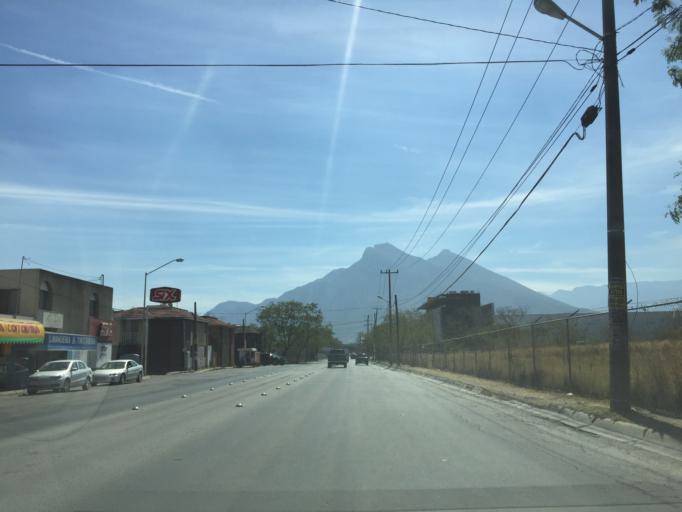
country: MX
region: Nuevo Leon
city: Guadalupe
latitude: 25.6978
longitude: -100.2399
